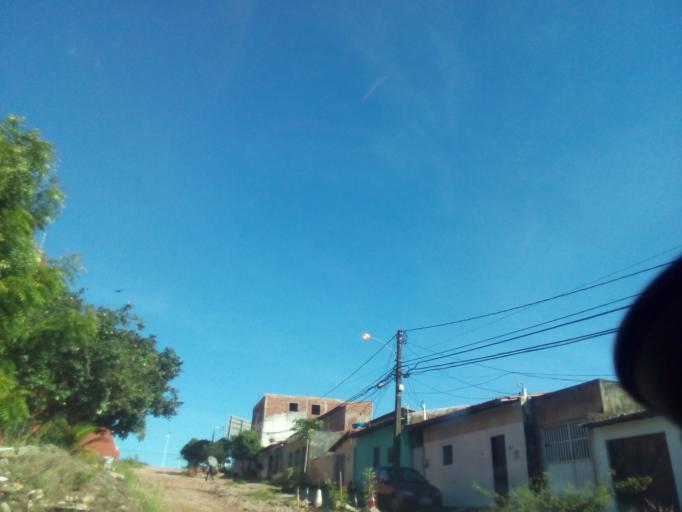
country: BR
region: Rio Grande do Norte
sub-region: Parnamirim
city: Parnamirim
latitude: -5.8654
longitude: -35.2145
